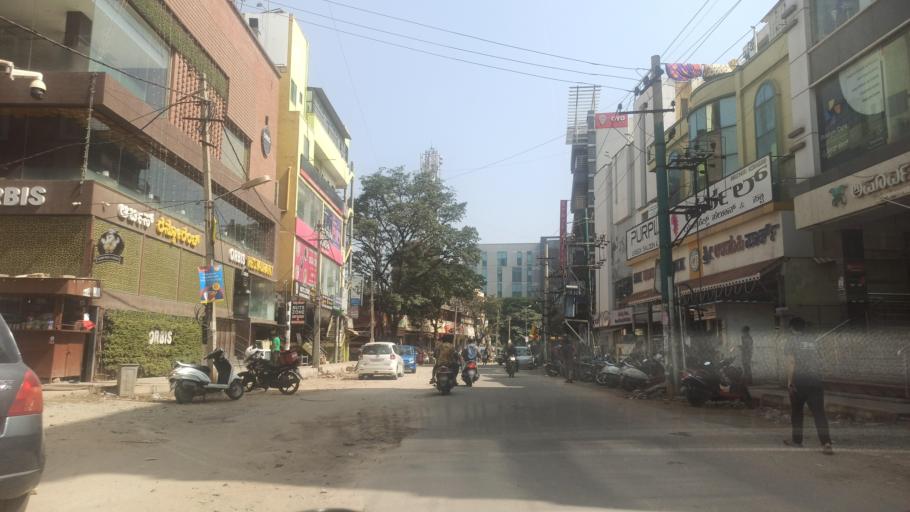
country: IN
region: Karnataka
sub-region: Bangalore Urban
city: Bangalore
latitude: 12.9648
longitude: 77.7170
